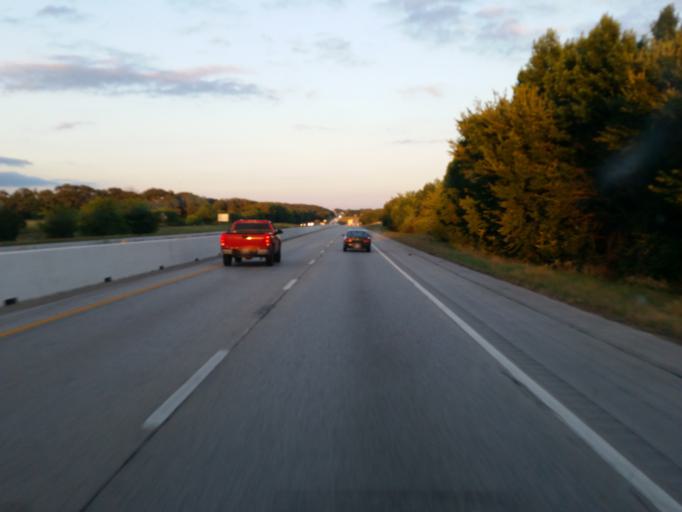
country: US
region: Texas
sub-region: Smith County
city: Hideaway
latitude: 32.4901
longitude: -95.5498
